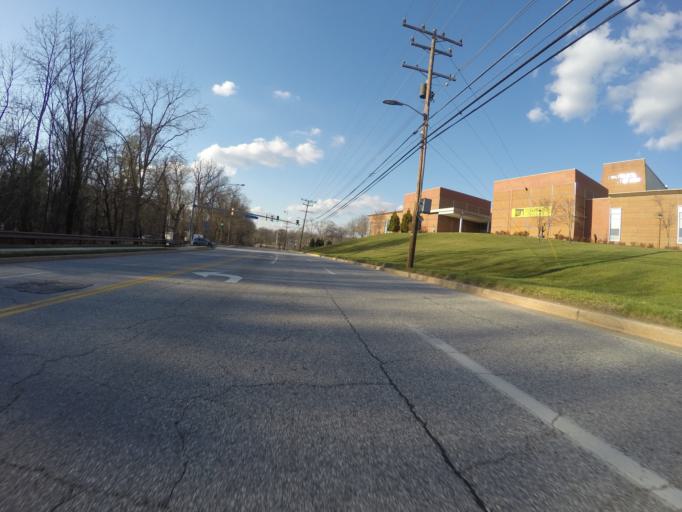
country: US
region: Maryland
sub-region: Baltimore County
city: Towson
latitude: 39.3896
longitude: -76.6131
